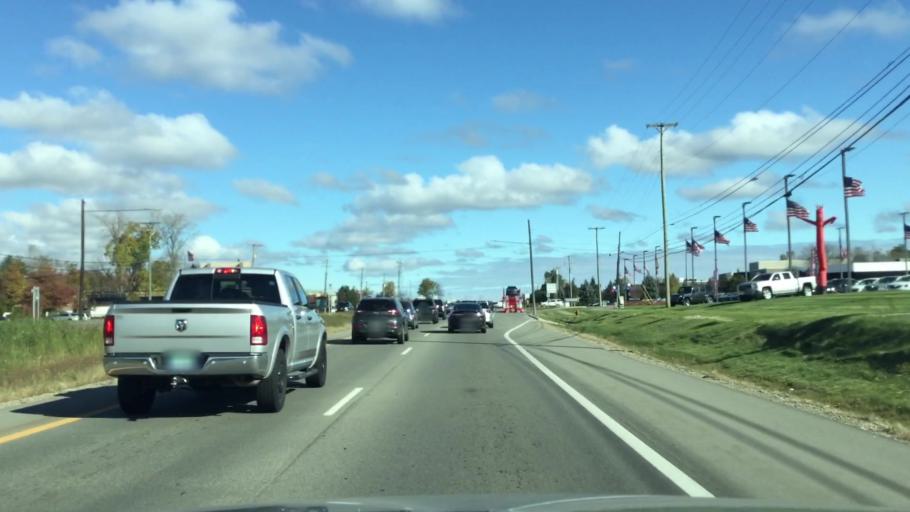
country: US
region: Michigan
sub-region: Oakland County
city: Lake Orion
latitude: 42.7586
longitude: -83.2449
